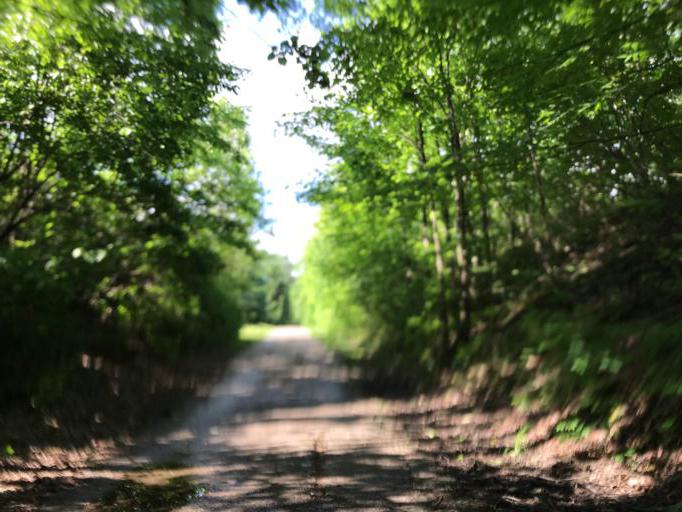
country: US
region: Michigan
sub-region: Oakland County
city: South Lyon
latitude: 42.4647
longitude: -83.6467
